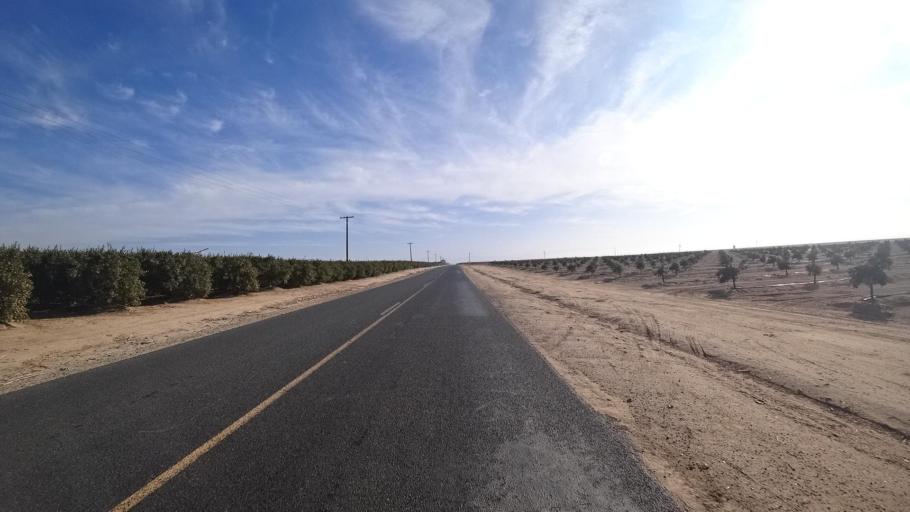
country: US
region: California
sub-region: Kern County
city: McFarland
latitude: 35.6021
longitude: -119.1201
